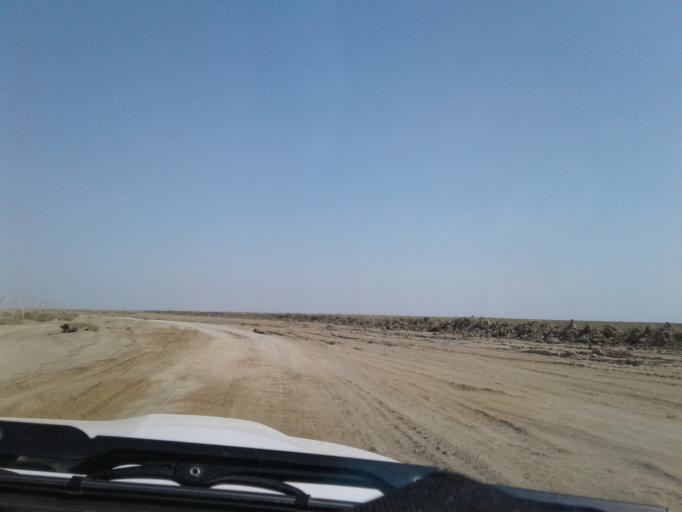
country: IR
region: Golestan
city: Gomishan
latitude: 37.8200
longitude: 53.9224
